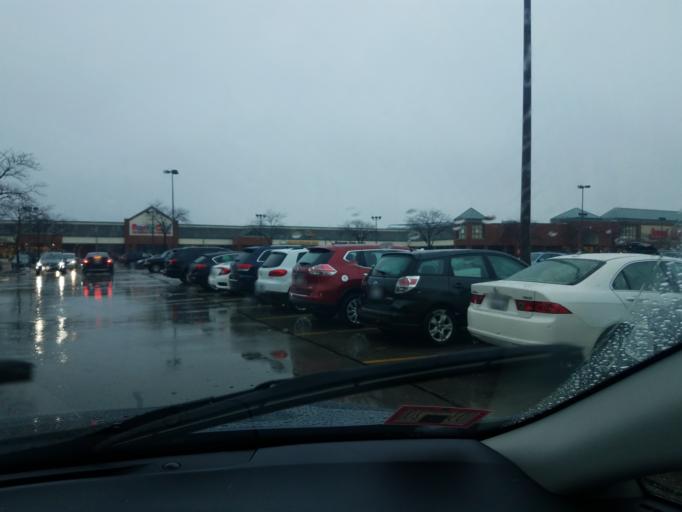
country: US
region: Illinois
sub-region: Cook County
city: Morton Grove
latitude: 42.0099
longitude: -87.7676
